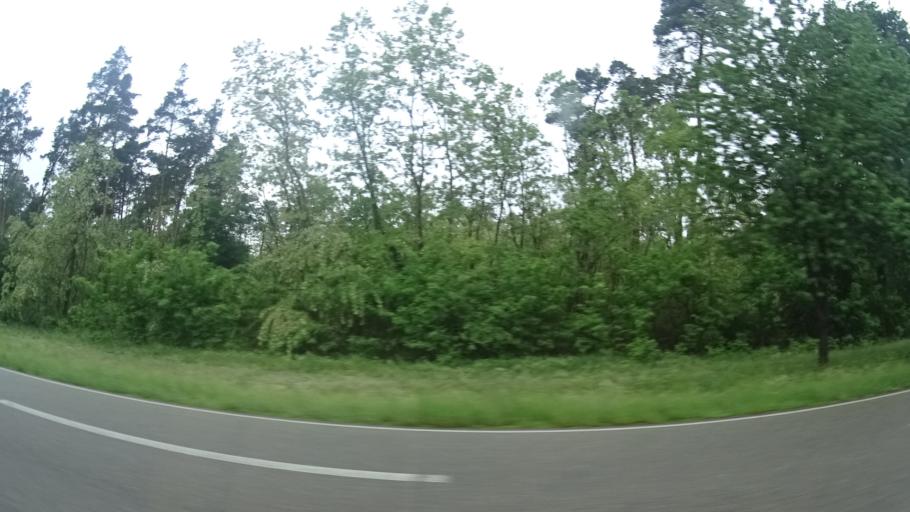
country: DE
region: Rheinland-Pfalz
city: Germersheim
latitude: 49.2046
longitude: 8.3460
